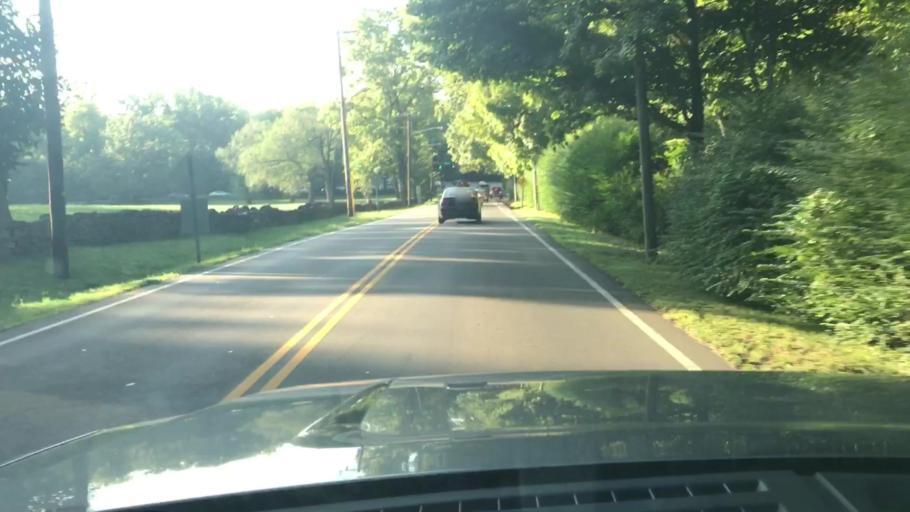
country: US
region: Tennessee
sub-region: Davidson County
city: Belle Meade
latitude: 36.1205
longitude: -86.8502
